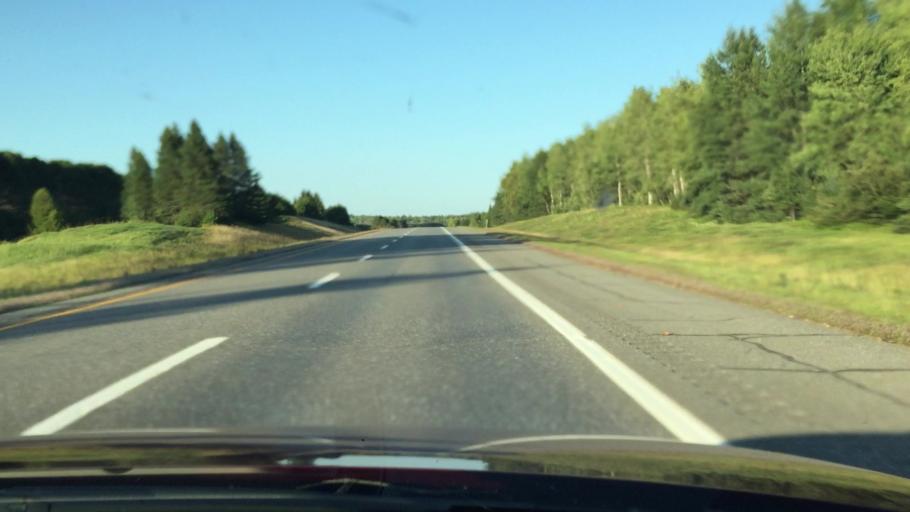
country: US
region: Maine
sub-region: Aroostook County
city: Hodgdon
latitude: 46.1381
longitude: -68.0759
